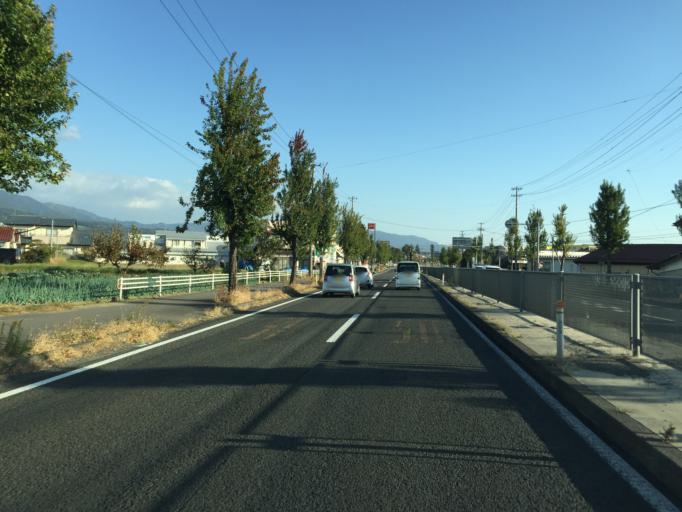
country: JP
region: Fukushima
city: Hobaramachi
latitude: 37.8207
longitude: 140.5052
